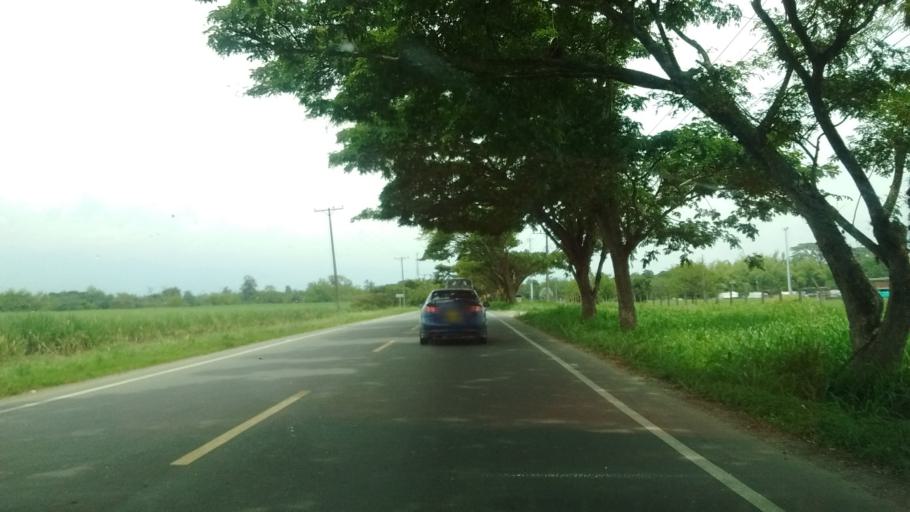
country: CO
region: Valle del Cauca
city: Jamundi
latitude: 3.2967
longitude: -76.4724
